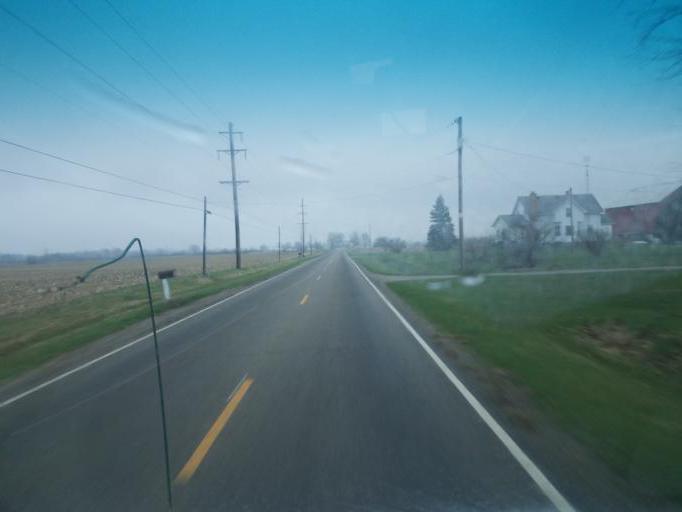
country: US
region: Ohio
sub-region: Defiance County
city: Hicksville
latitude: 41.3423
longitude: -84.7670
